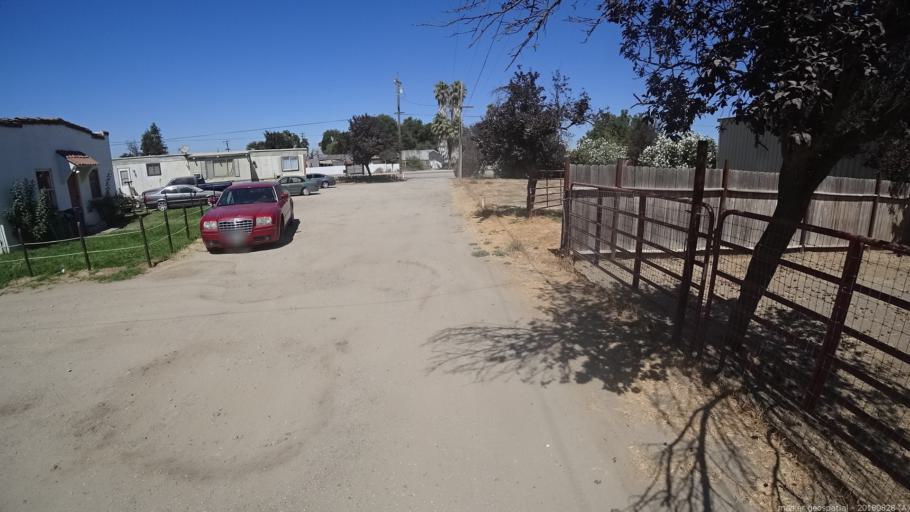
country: US
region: California
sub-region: San Luis Obispo County
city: Lake Nacimiento
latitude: 36.0204
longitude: -120.9045
